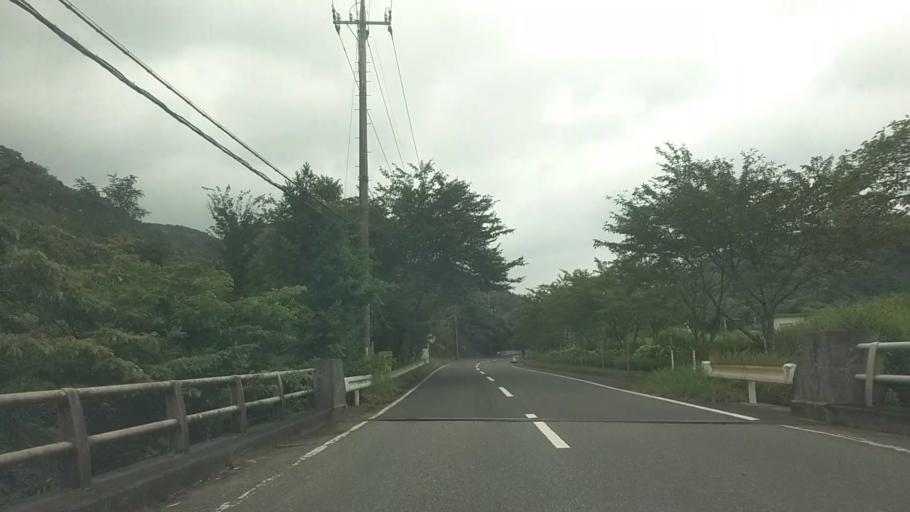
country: JP
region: Chiba
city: Kimitsu
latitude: 35.2246
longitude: 139.9537
